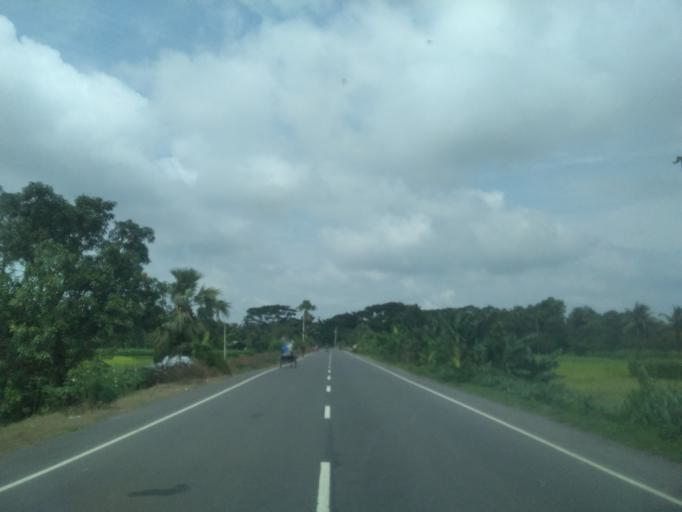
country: BD
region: Khulna
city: Kesabpur
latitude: 22.8200
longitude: 89.2638
